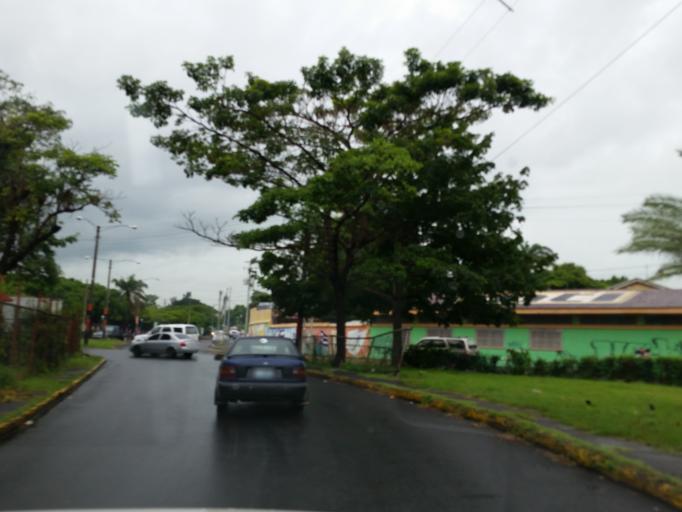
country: NI
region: Managua
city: Managua
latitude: 12.1517
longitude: -86.2824
